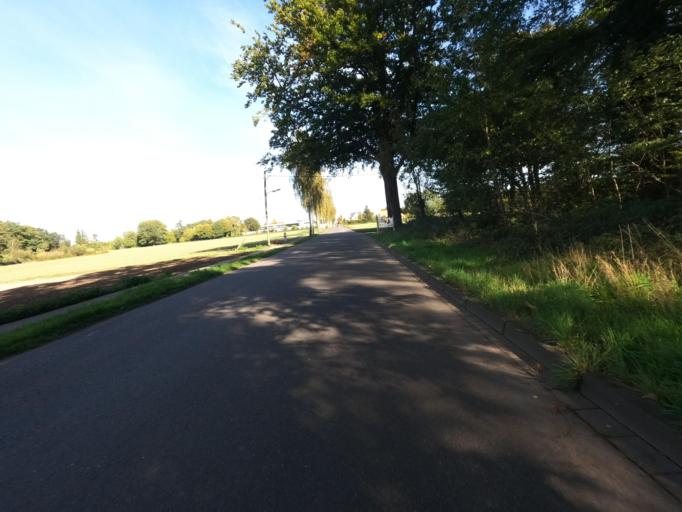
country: DE
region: North Rhine-Westphalia
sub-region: Regierungsbezirk Koln
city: Wassenberg
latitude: 51.0981
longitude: 6.1759
